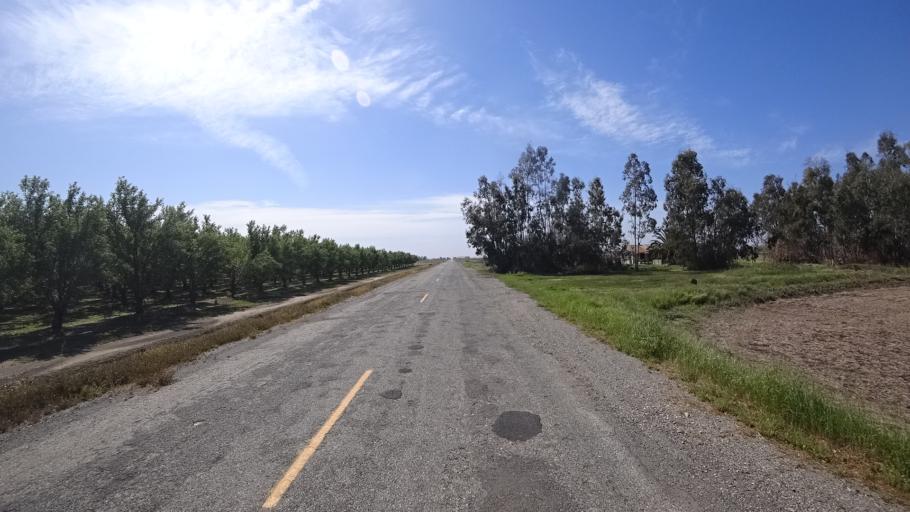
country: US
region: California
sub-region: Glenn County
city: Hamilton City
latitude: 39.6105
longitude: -122.0463
